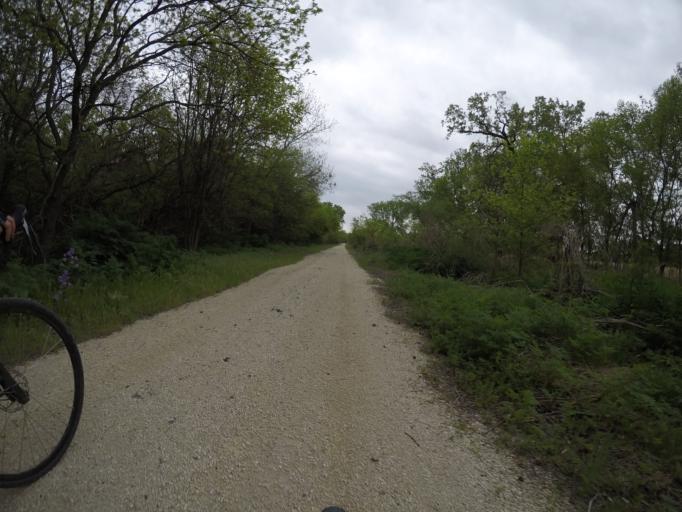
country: US
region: Nebraska
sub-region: Gage County
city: Wymore
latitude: 40.1166
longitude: -96.6321
